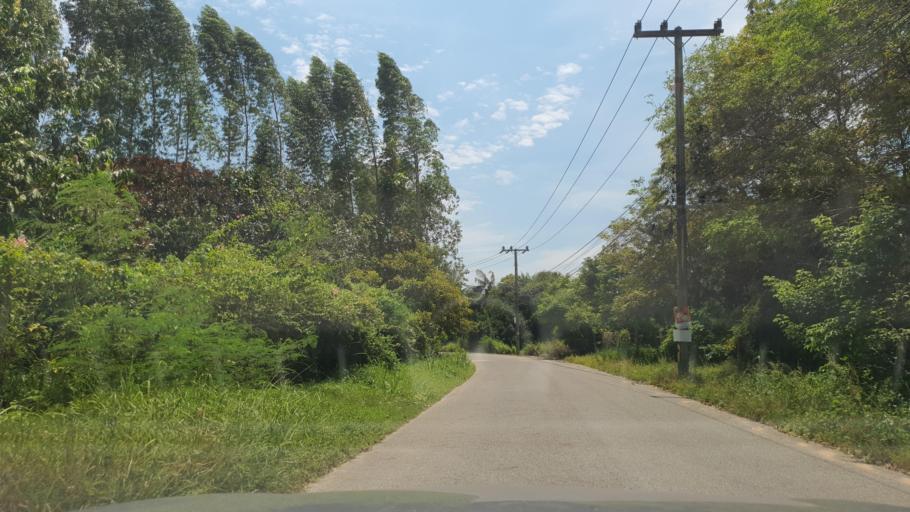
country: TH
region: Rayong
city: Ban Chang
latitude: 12.8008
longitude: 100.9469
